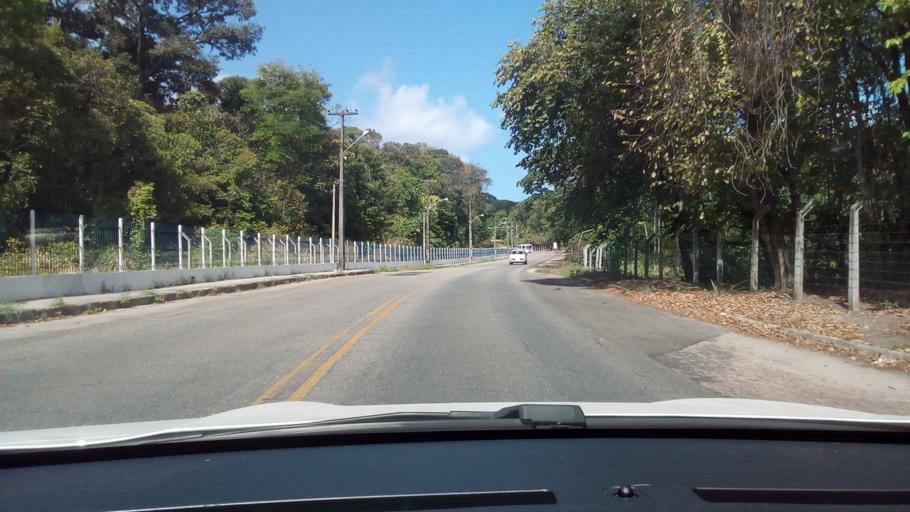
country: BR
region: Paraiba
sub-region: Joao Pessoa
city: Joao Pessoa
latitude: -7.1430
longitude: -34.8481
